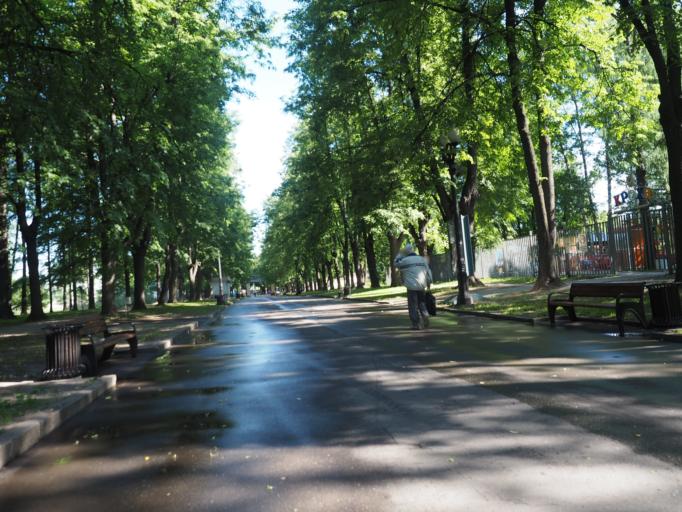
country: RU
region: Moscow
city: Ryazanskiy
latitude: 55.7748
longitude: 37.7488
